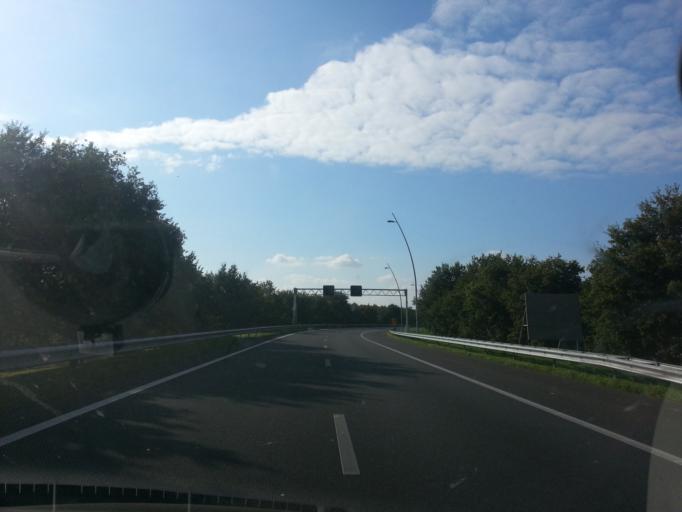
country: NL
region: North Brabant
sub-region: Gemeente Best
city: Best
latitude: 51.4928
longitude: 5.4357
